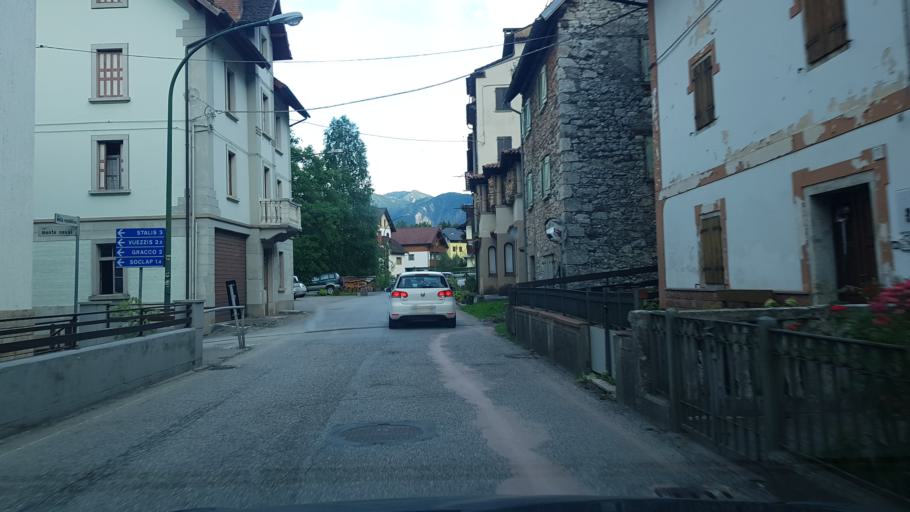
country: IT
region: Friuli Venezia Giulia
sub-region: Provincia di Udine
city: Rigolato
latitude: 46.5510
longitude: 12.8530
